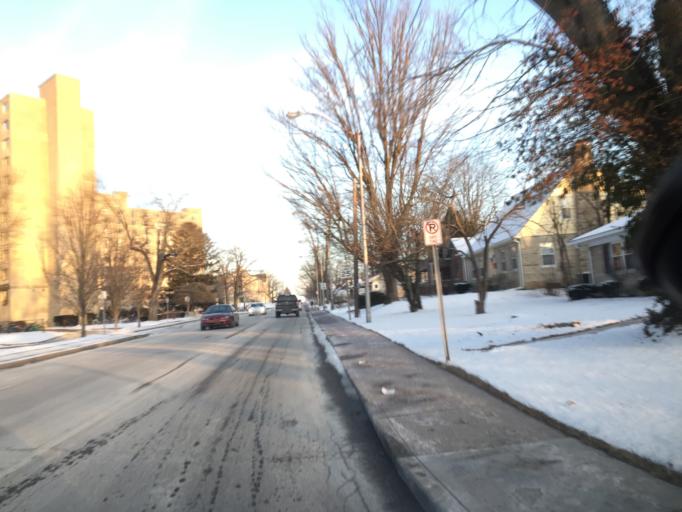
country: US
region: Indiana
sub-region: Monroe County
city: Bloomington
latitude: 39.1642
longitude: -86.5141
